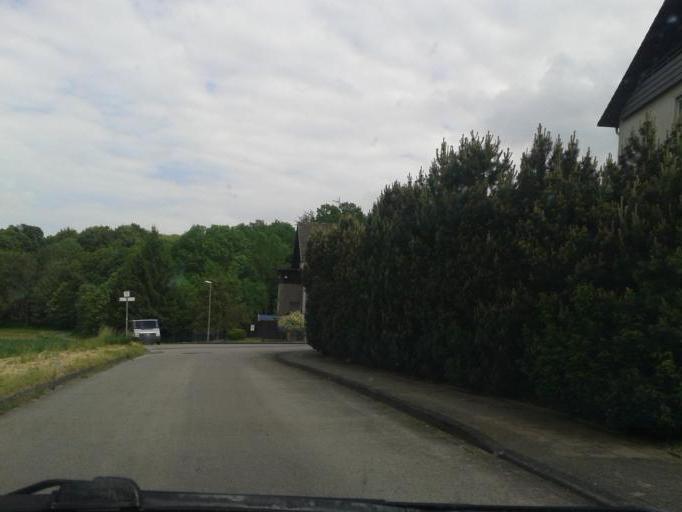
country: DE
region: North Rhine-Westphalia
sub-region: Regierungsbezirk Detmold
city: Schieder-Schwalenberg
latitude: 51.9178
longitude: 9.1599
